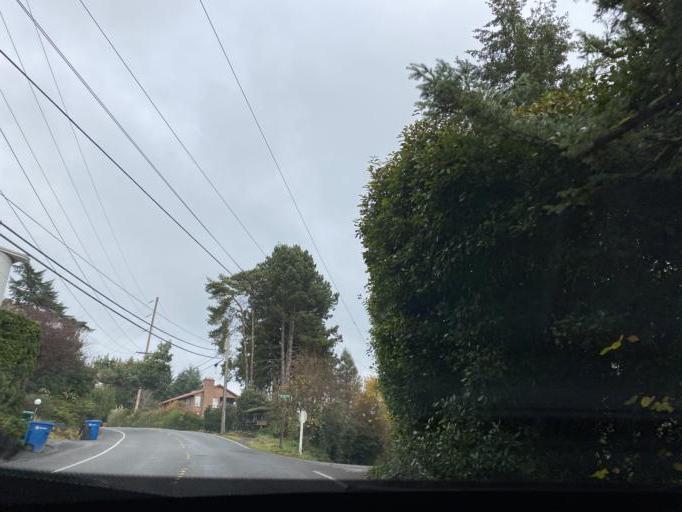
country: US
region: Washington
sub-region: King County
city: Mercer Island
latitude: 47.5375
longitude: -122.2126
